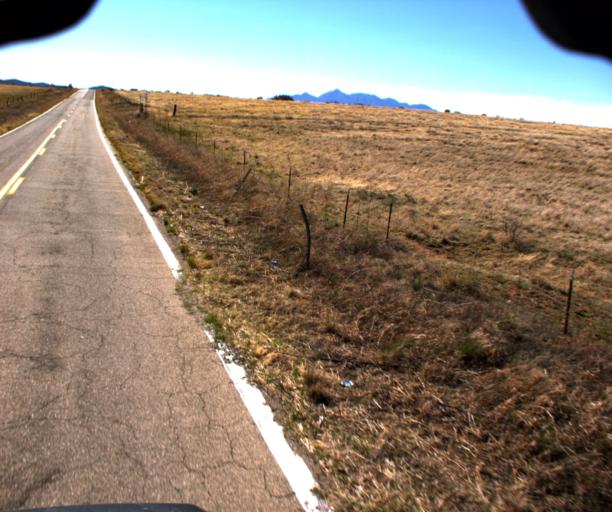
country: US
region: Arizona
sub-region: Cochise County
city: Huachuca City
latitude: 31.6008
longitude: -110.5703
